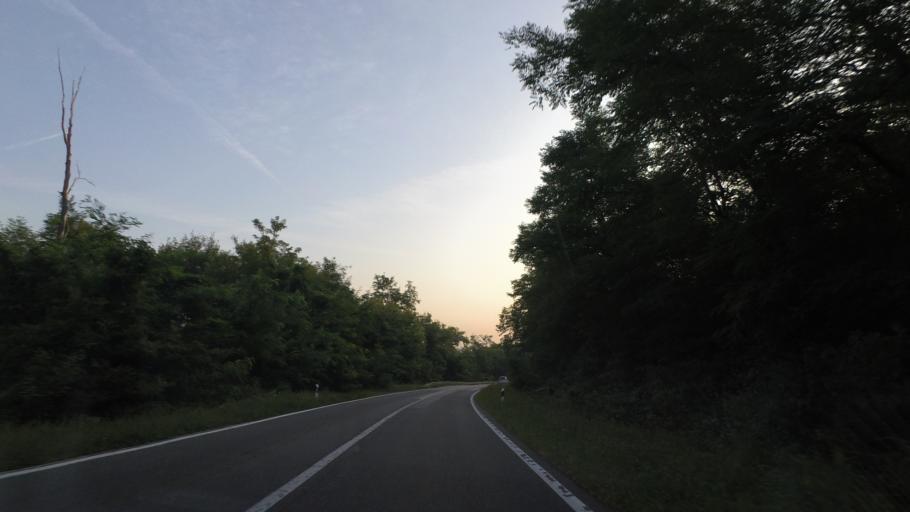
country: HR
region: Brodsko-Posavska
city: Cernik
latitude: 45.2845
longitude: 17.4050
